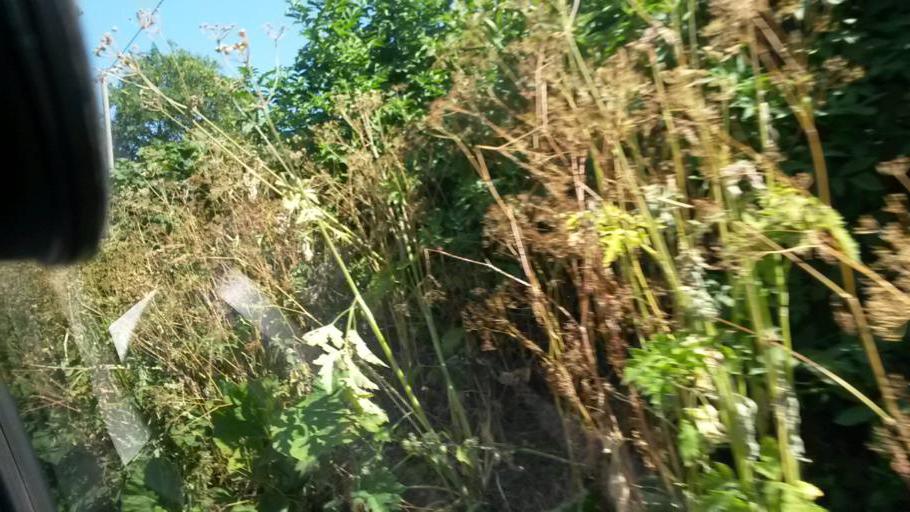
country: IE
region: Leinster
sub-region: Fingal County
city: Swords
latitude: 53.4904
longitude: -6.2770
